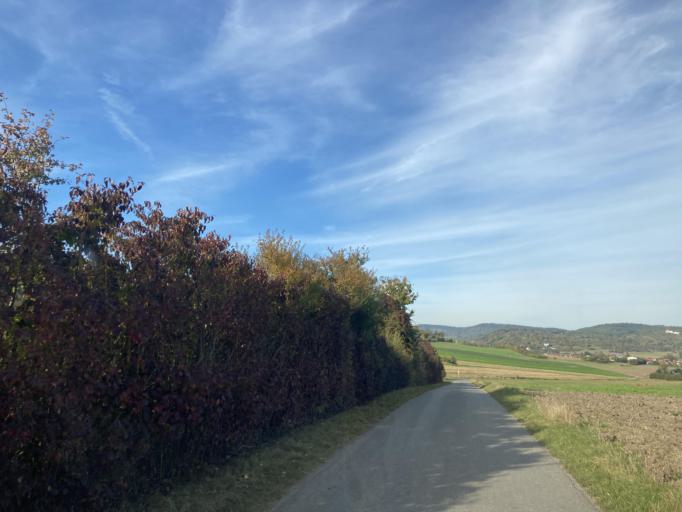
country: DE
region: Baden-Wuerttemberg
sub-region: Tuebingen Region
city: Rottenburg
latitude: 48.5134
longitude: 8.9620
